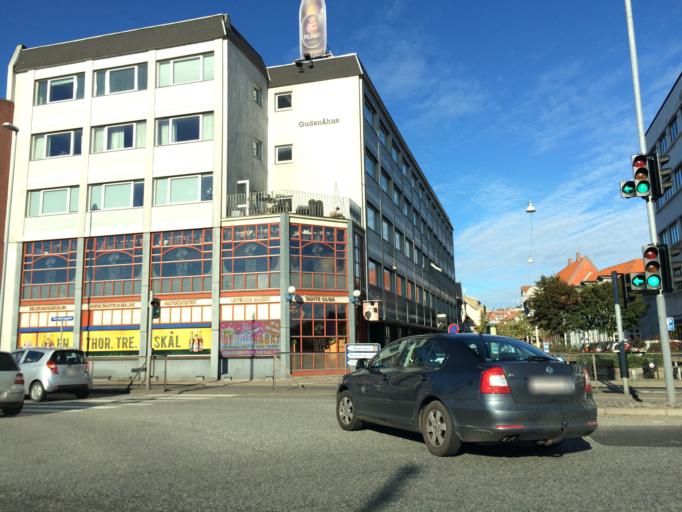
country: DK
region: Central Jutland
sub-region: Randers Kommune
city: Randers
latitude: 56.4570
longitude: 10.0392
